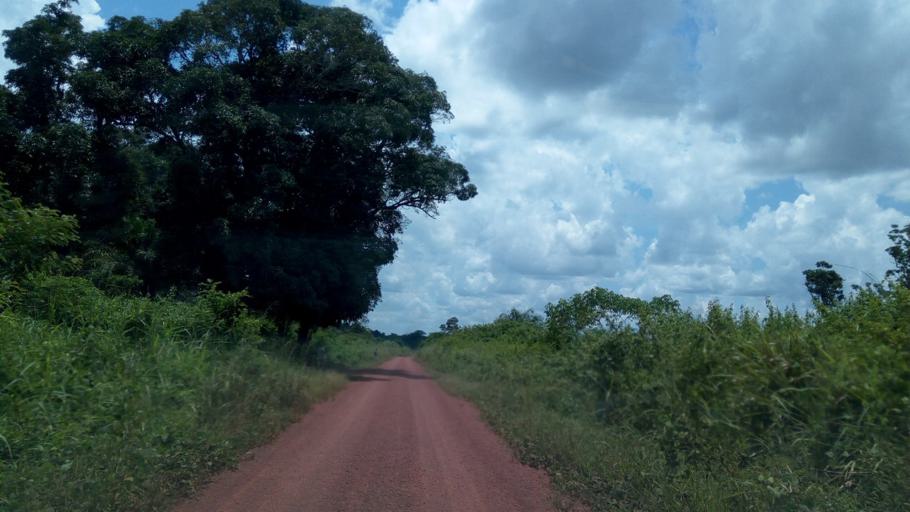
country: CD
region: Equateur
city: Libenge
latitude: 3.7718
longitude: 18.9495
